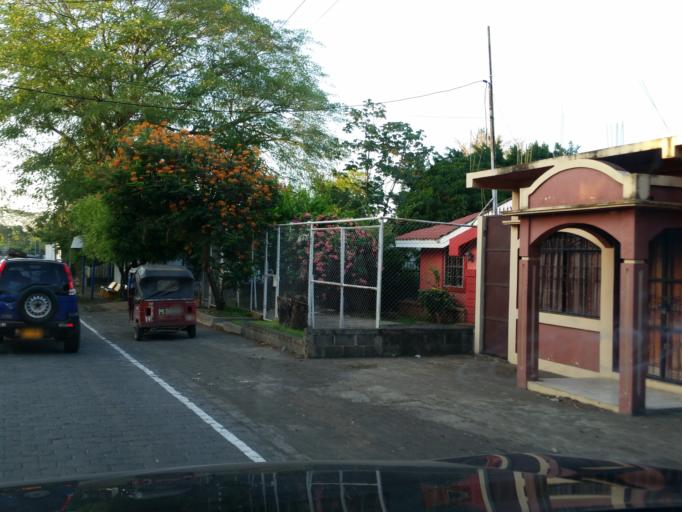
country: NI
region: Masaya
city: Ticuantepe
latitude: 12.0456
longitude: -86.2018
